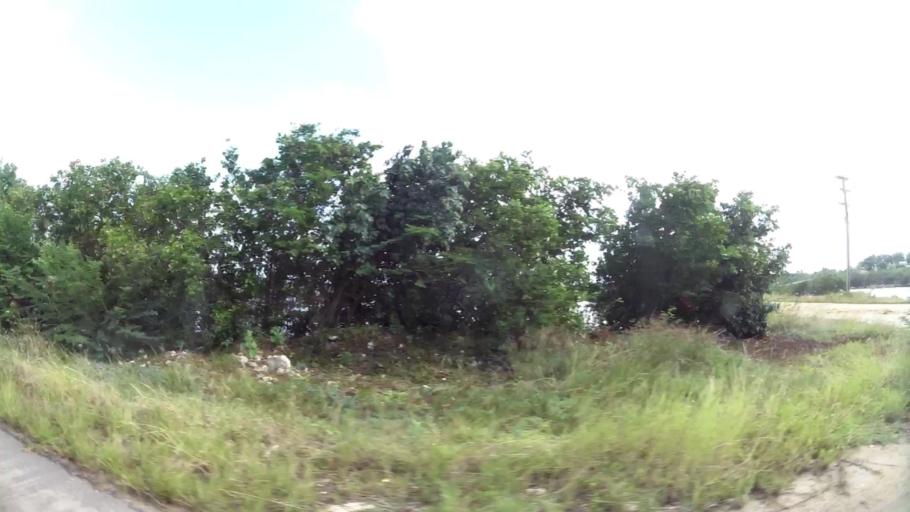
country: AG
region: Saint John
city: Saint John's
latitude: 17.1432
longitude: -61.8575
